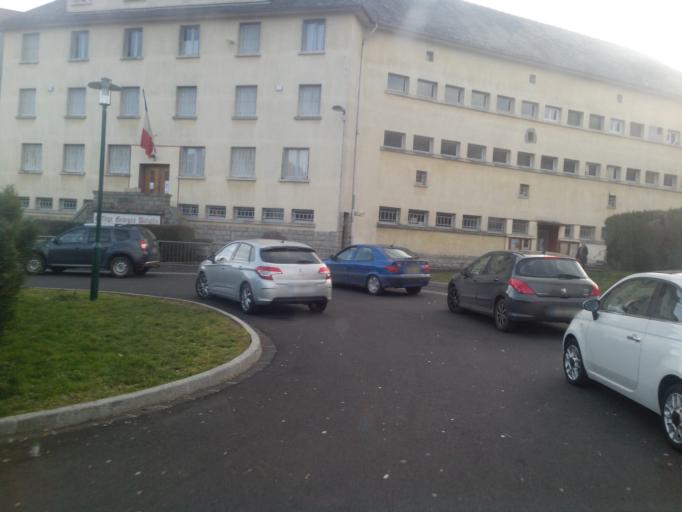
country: FR
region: Auvergne
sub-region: Departement du Cantal
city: Riom-es-Montagnes
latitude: 45.2817
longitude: 2.6612
